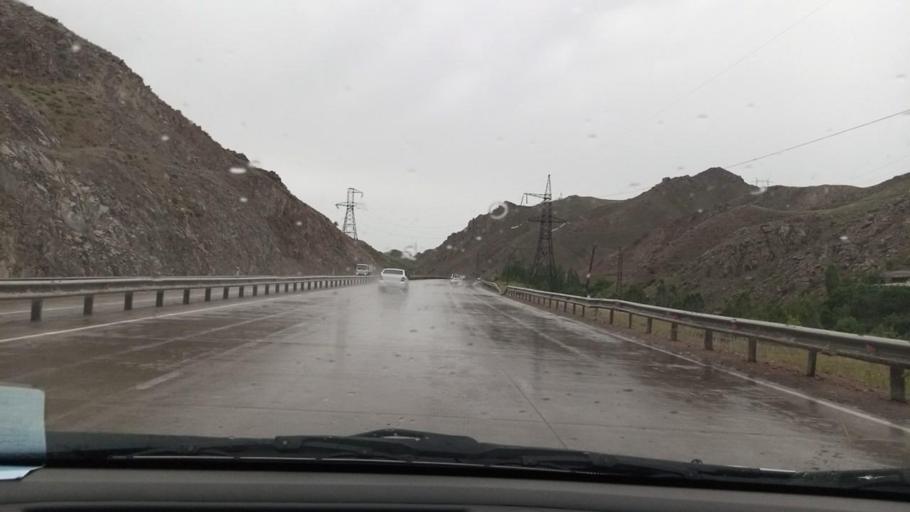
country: TJ
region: Viloyati Sughd
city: Shaydon
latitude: 40.9657
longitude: 70.6587
